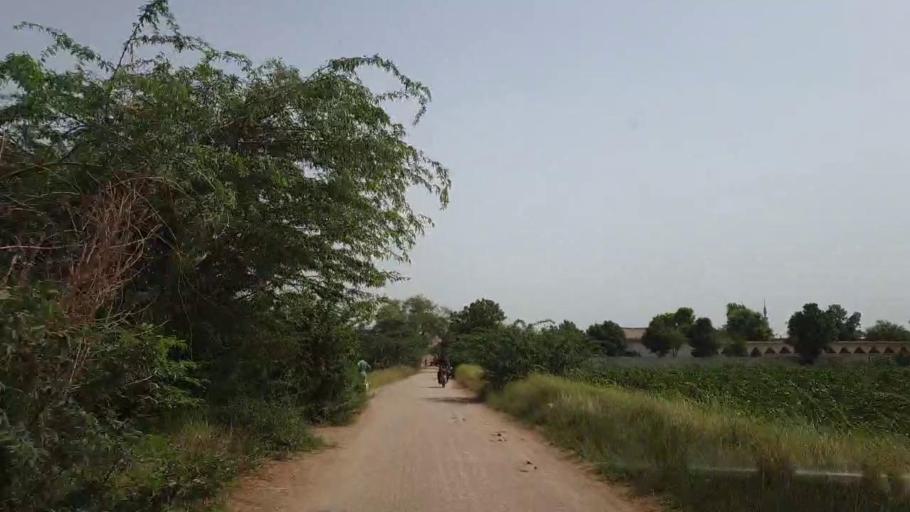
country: PK
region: Sindh
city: Sakrand
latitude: 26.1147
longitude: 68.3976
